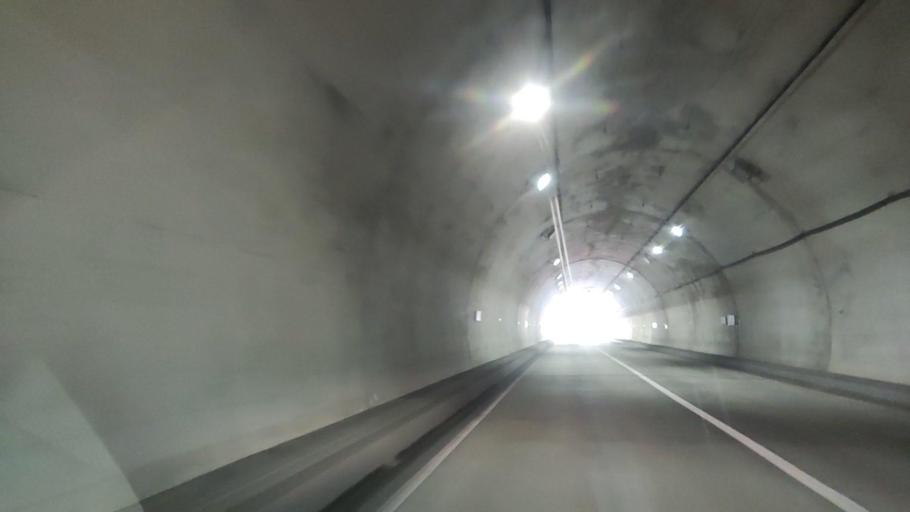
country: JP
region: Hokkaido
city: Ishikari
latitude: 43.5160
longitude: 141.3880
